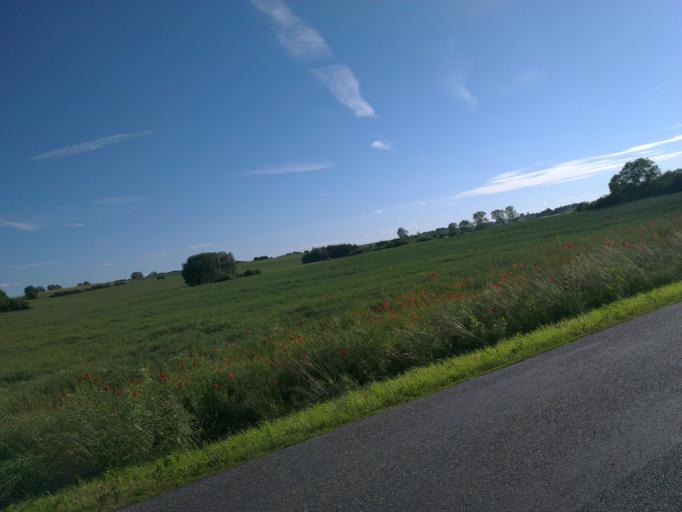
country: DK
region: Capital Region
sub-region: Frederikssund Kommune
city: Skibby
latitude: 55.7601
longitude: 12.0347
